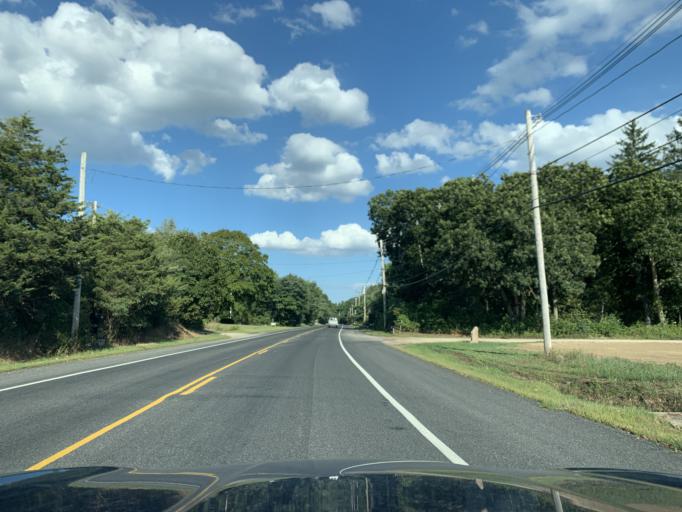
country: US
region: Rhode Island
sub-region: Washington County
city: Kingston
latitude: 41.4765
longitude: -71.6076
